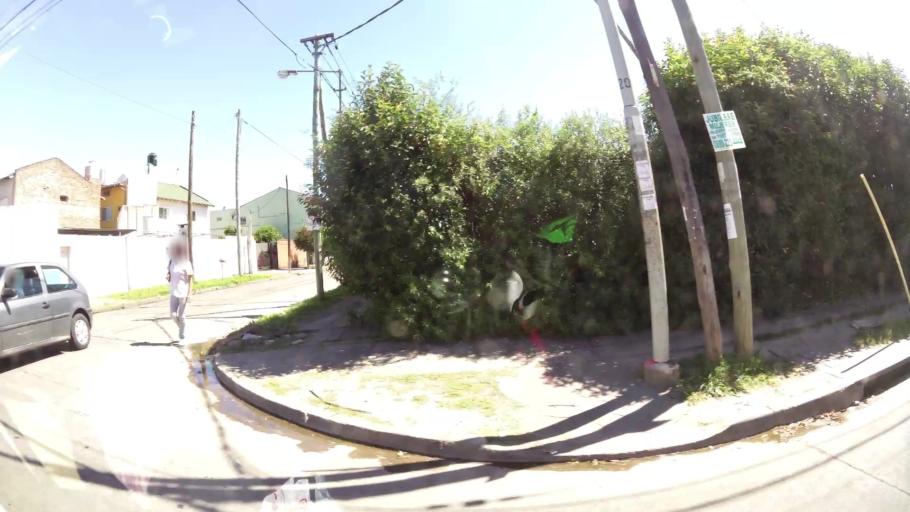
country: AR
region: Buenos Aires
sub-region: Partido de General San Martin
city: General San Martin
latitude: -34.5261
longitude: -58.5588
